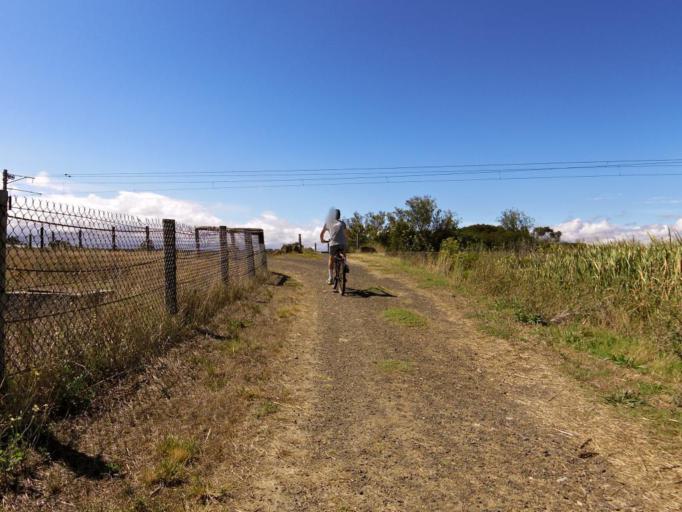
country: AU
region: Victoria
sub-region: Hobsons Bay
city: Altona
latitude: -37.8648
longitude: 144.8073
